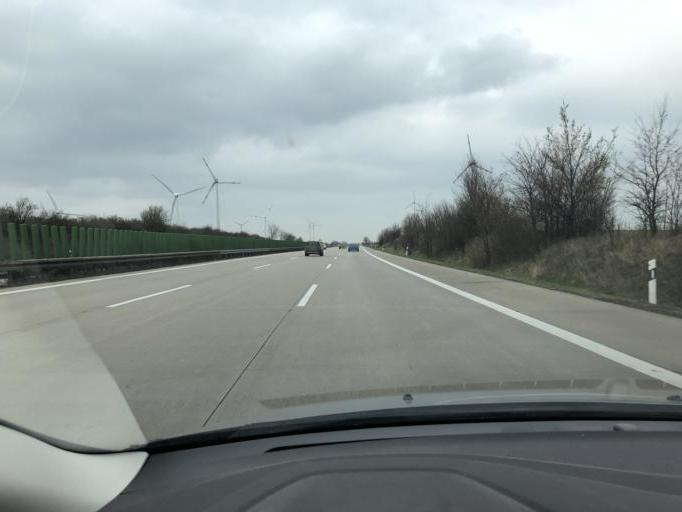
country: DE
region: Saxony-Anhalt
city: Prittitz
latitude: 51.1272
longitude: 11.9606
